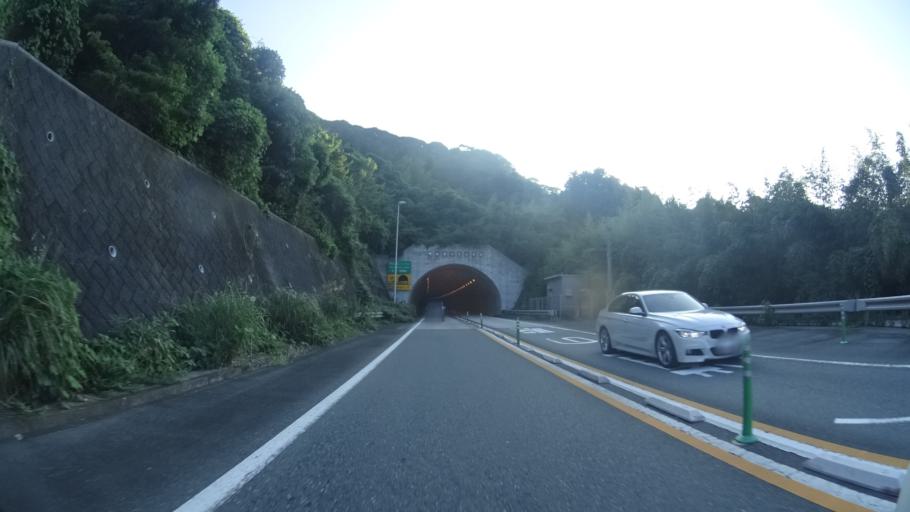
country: JP
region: Yamaguchi
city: Hagi
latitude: 34.3870
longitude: 131.3196
